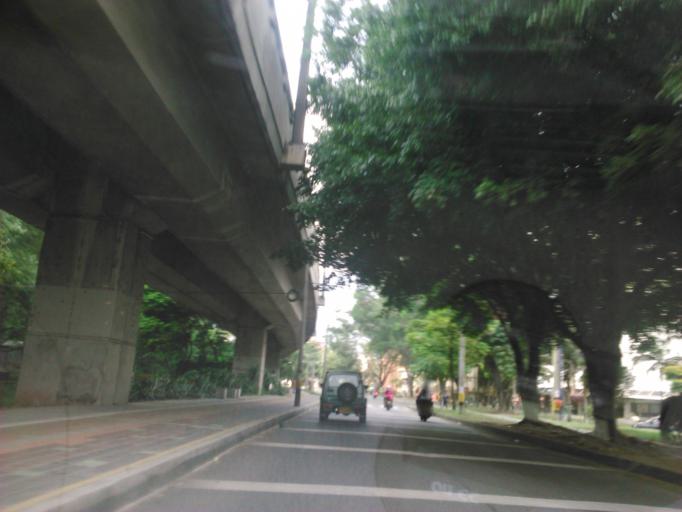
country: CO
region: Antioquia
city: Medellin
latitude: 6.2559
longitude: -75.5923
